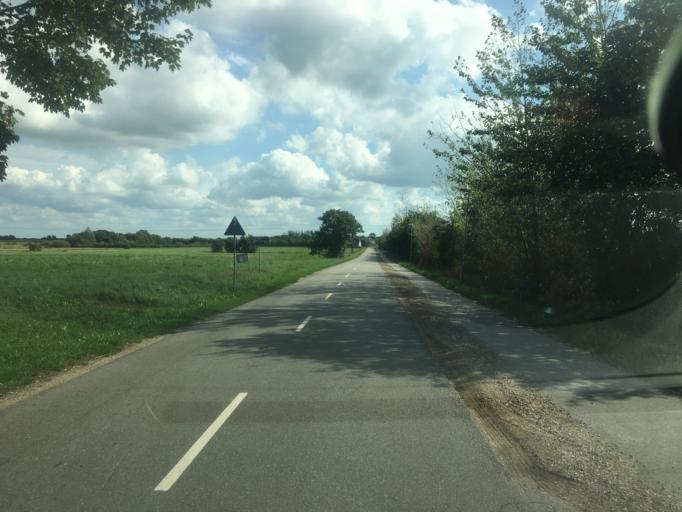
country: DE
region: Schleswig-Holstein
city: Ellhoft
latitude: 54.9463
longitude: 8.9660
